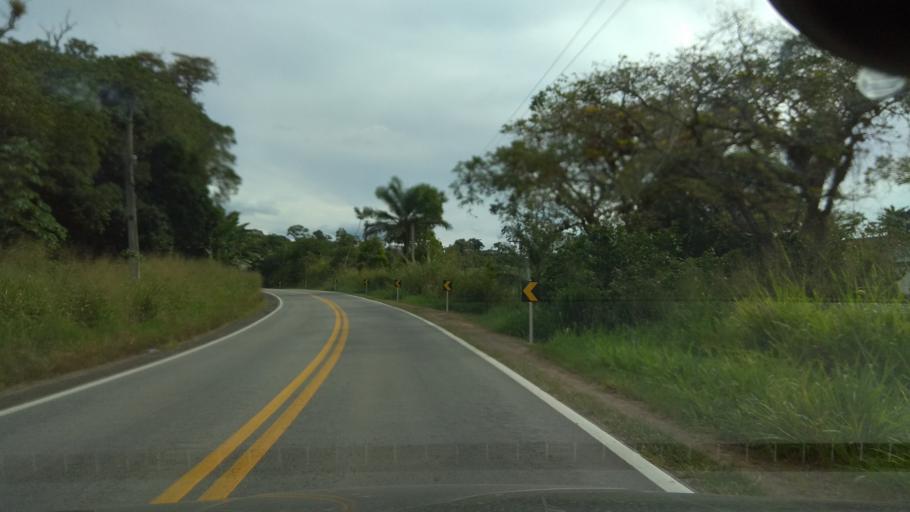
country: BR
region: Bahia
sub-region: Ubata
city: Ubata
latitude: -14.1931
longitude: -39.5601
